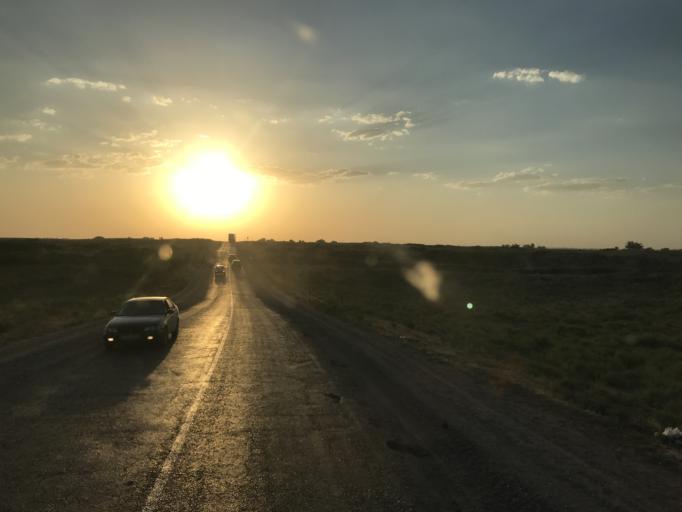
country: UZ
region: Toshkent
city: Yangiyul
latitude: 41.3363
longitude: 68.8840
